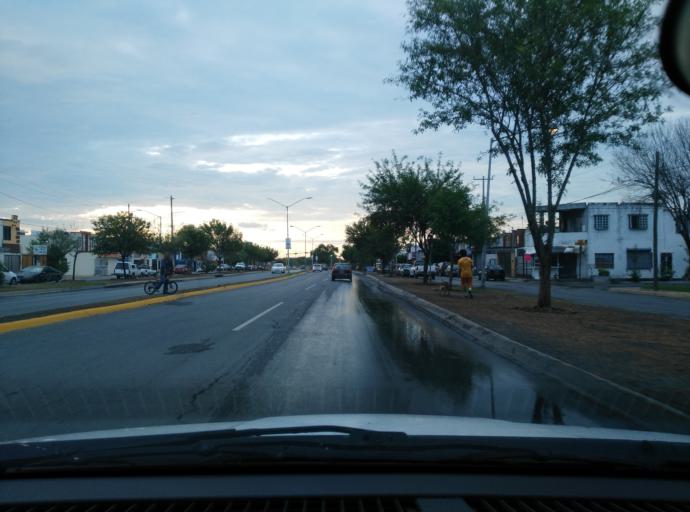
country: MX
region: Nuevo Leon
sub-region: Apodaca
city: Fraccionamiento Cosmopolis Octavo Sector
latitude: 25.7678
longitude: -100.2439
